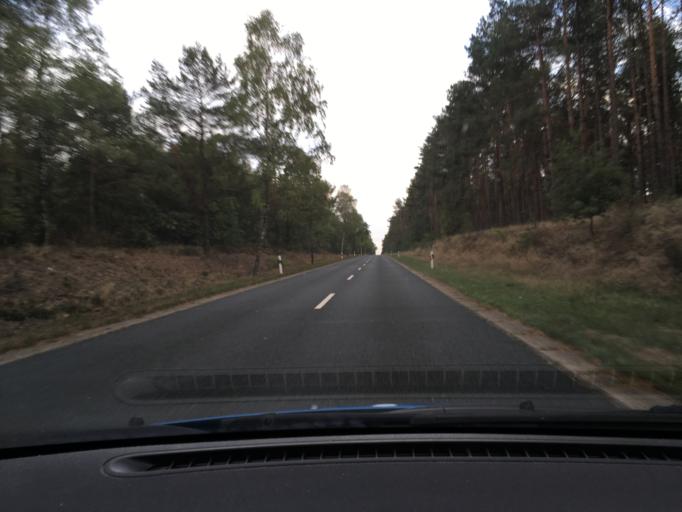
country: DE
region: Lower Saxony
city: Bispingen
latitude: 53.0842
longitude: 10.0555
